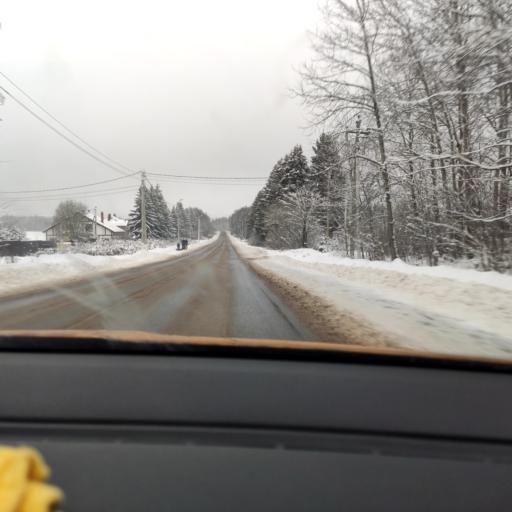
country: RU
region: Moskovskaya
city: Yershovo
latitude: 55.7724
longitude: 36.8572
